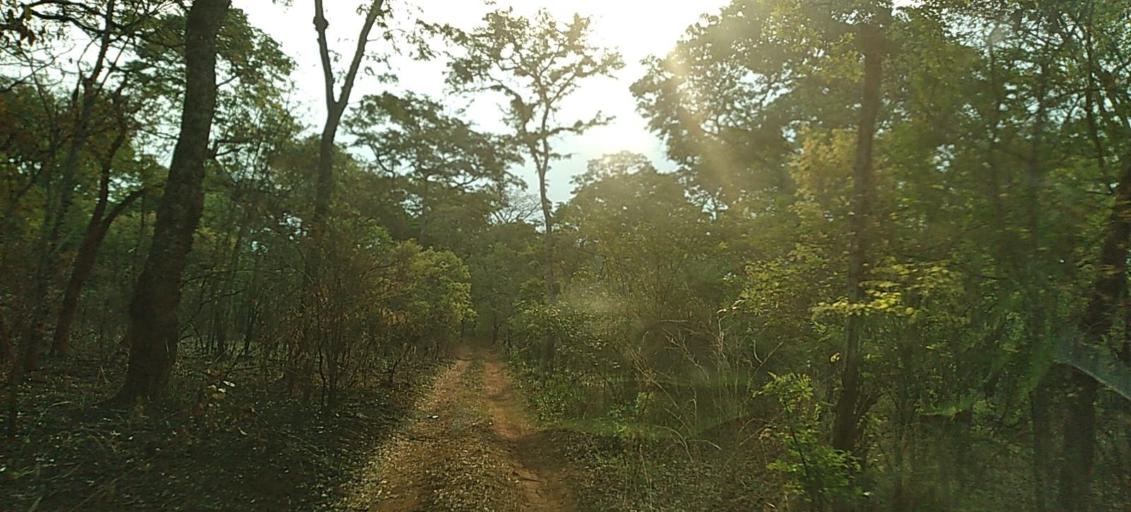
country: ZM
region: North-Western
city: Solwezi
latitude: -12.0415
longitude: 26.0364
